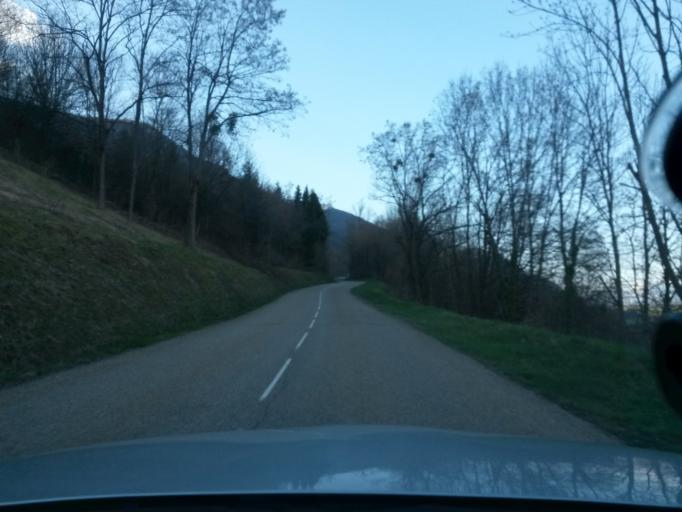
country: FR
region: Rhone-Alpes
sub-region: Departement de l'Isere
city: Le Touvet
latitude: 45.3499
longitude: 5.9414
